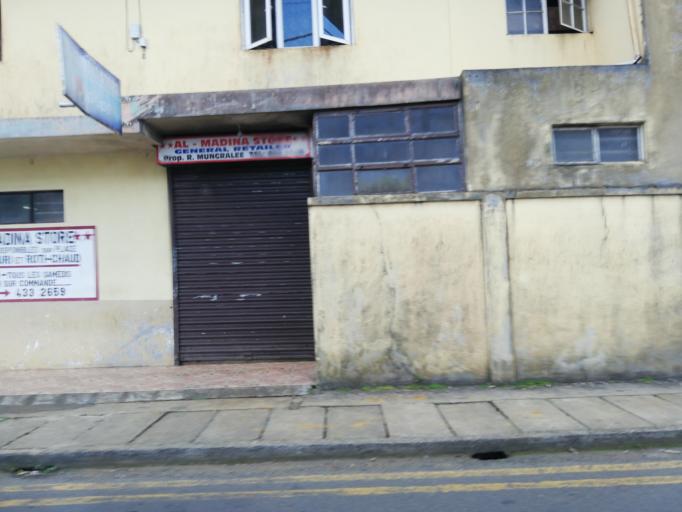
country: MU
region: Moka
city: Verdun
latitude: -20.2174
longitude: 57.5512
